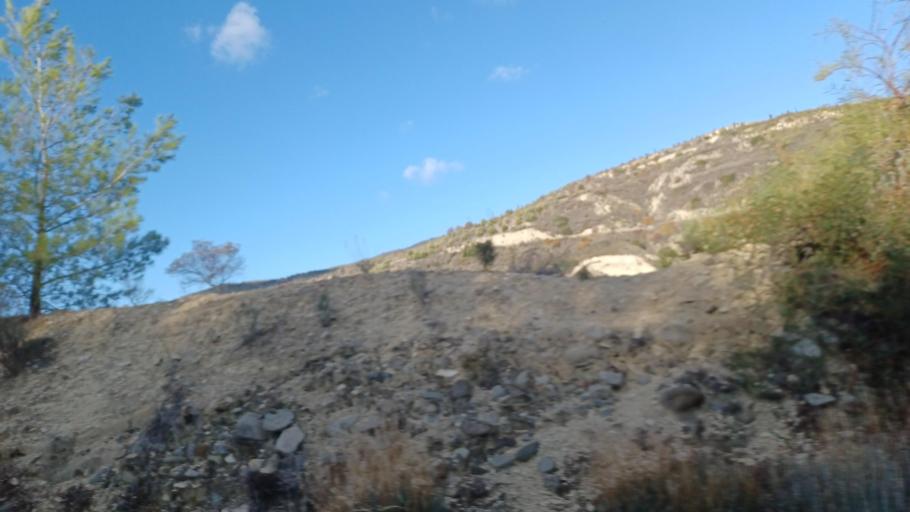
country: CY
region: Limassol
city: Pachna
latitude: 34.8554
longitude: 32.7286
